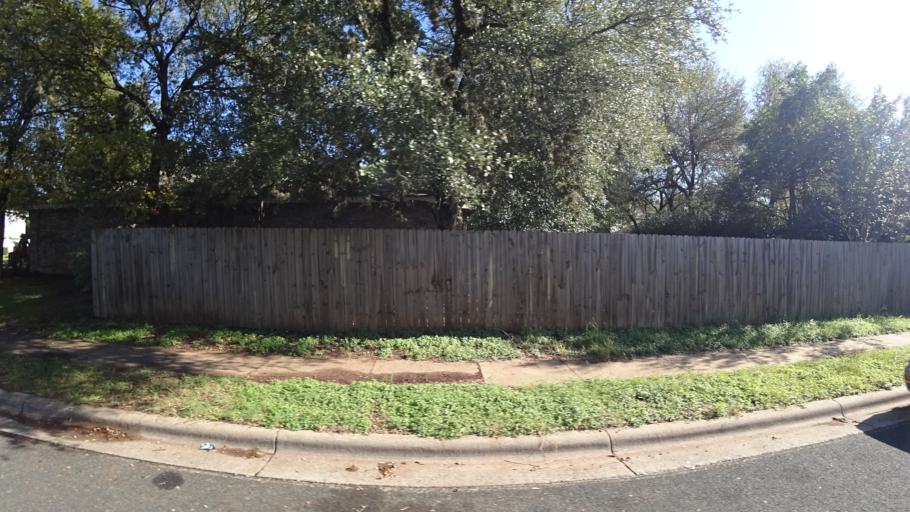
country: US
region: Texas
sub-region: Travis County
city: Shady Hollow
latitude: 30.2087
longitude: -97.8576
